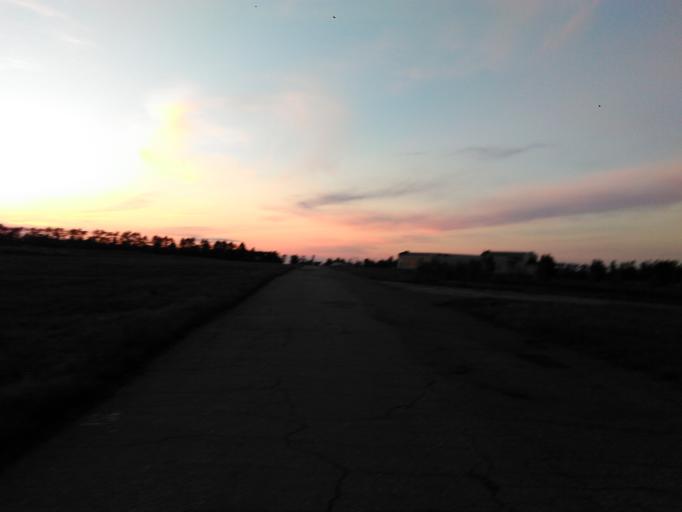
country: RU
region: Penza
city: Lermontovo
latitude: 52.9973
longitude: 43.6725
